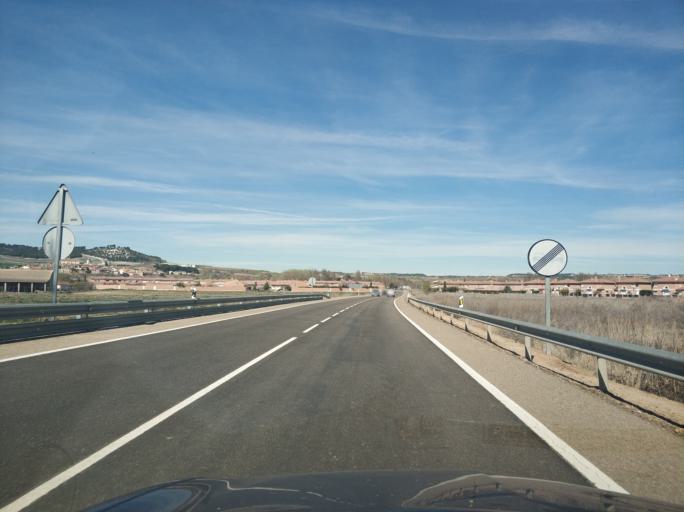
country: ES
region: Castille and Leon
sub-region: Provincia de Valladolid
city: Simancas
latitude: 41.5831
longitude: -4.8161
